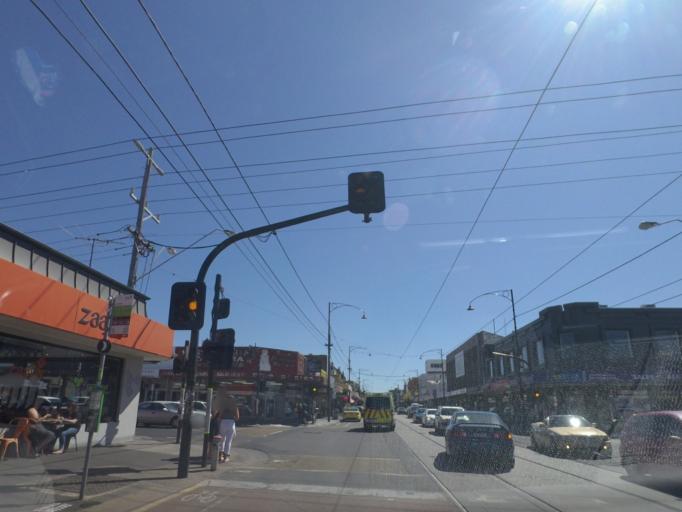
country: AU
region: Victoria
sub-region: Moreland
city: Coburg
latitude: -37.7452
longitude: 144.9658
